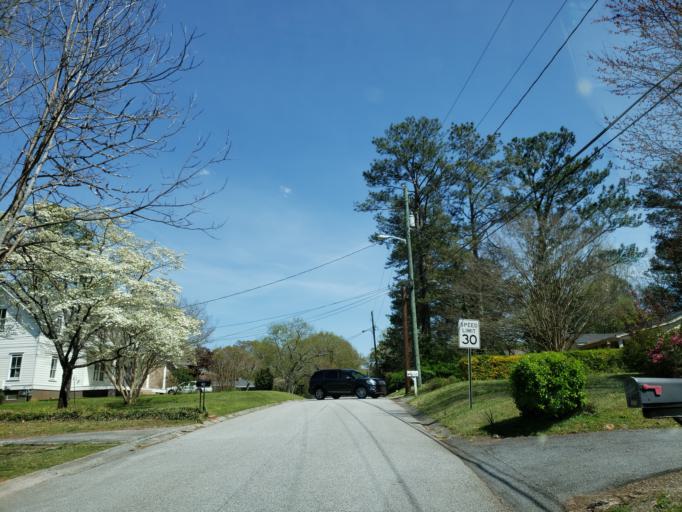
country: US
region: Georgia
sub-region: Cobb County
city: Marietta
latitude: 33.9584
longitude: -84.5631
